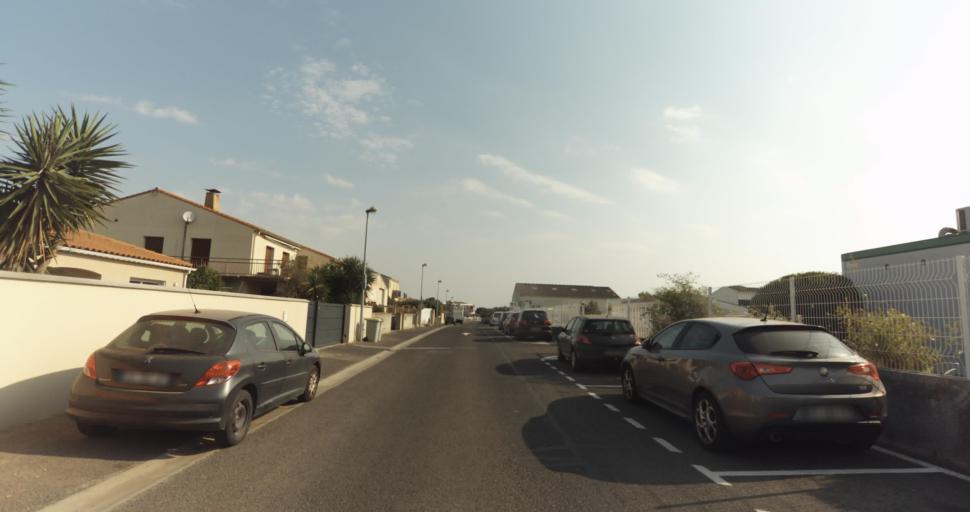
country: FR
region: Languedoc-Roussillon
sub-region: Departement des Pyrenees-Orientales
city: Latour-Bas-Elne
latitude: 42.6149
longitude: 2.9952
